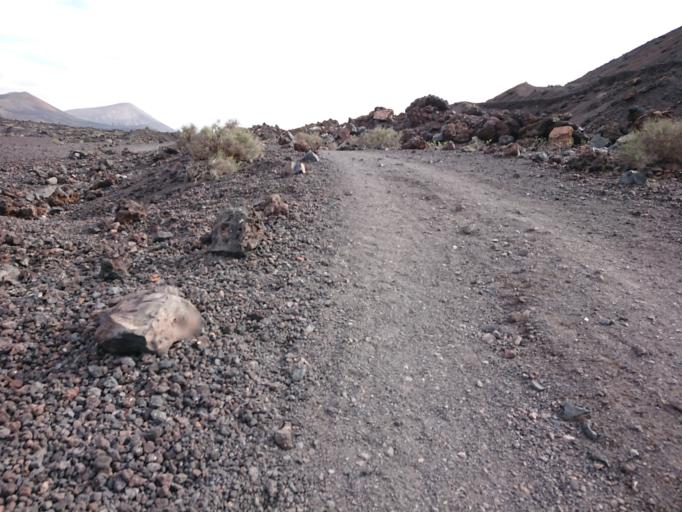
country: ES
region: Canary Islands
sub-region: Provincia de Las Palmas
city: Tinajo
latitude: 29.0093
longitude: -13.6772
